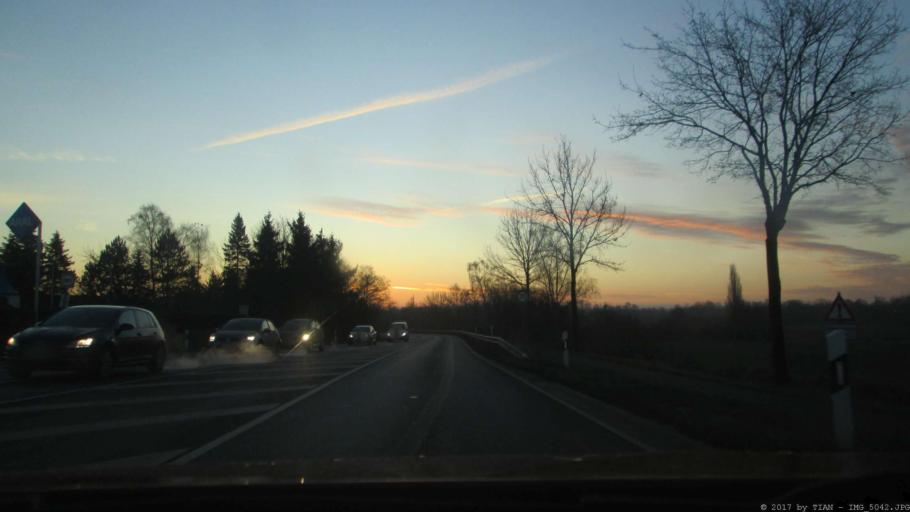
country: DE
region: Lower Saxony
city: Wolfsburg
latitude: 52.4381
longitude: 10.8293
